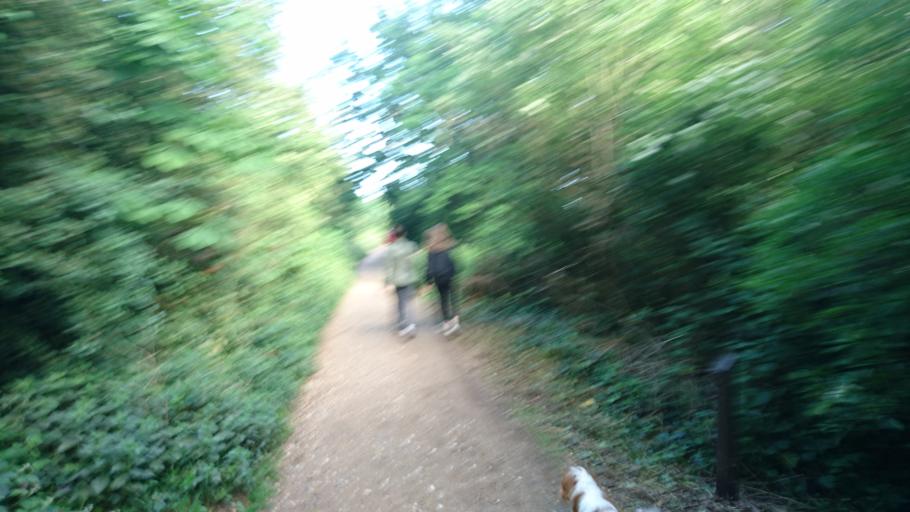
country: GB
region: England
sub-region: Greater London
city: Harringay
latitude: 51.5726
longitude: -0.1104
